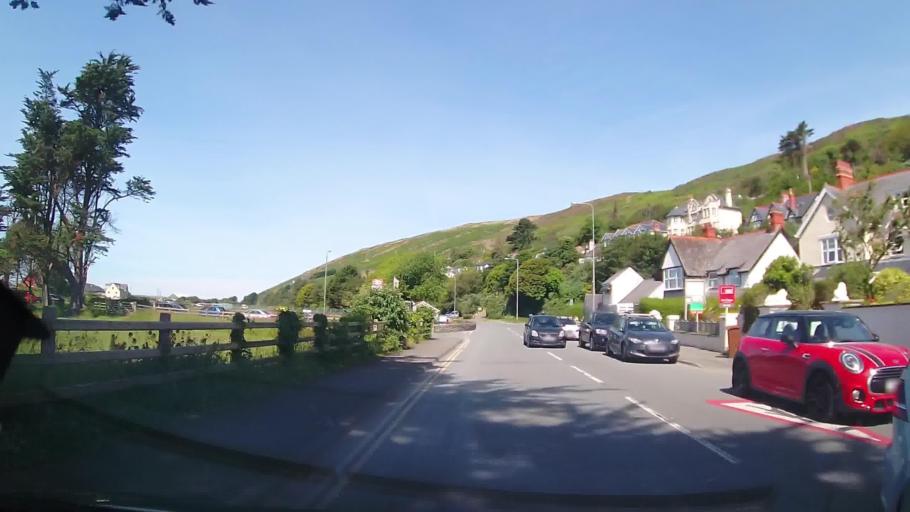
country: GB
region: Wales
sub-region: Gwynedd
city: Tywyn
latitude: 52.5447
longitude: -4.0528
